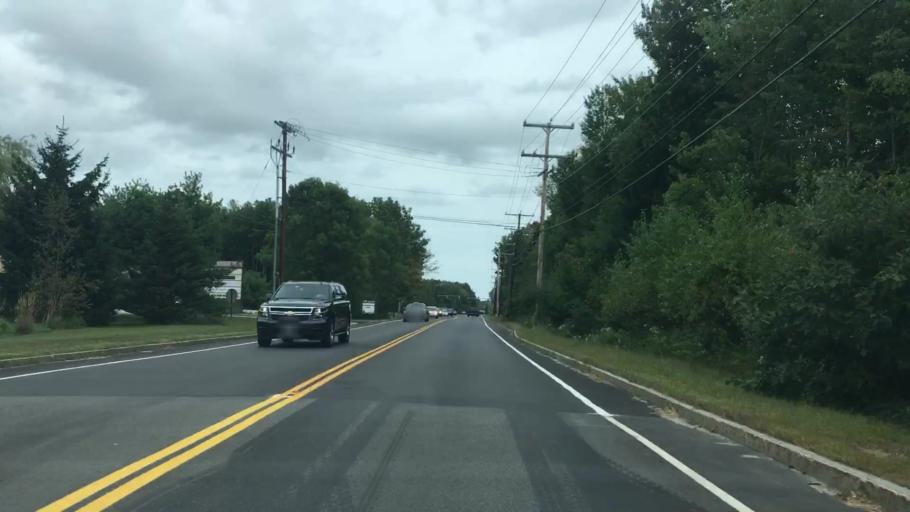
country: US
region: Maine
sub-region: Cumberland County
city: South Portland Gardens
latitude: 43.6196
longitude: -70.3430
